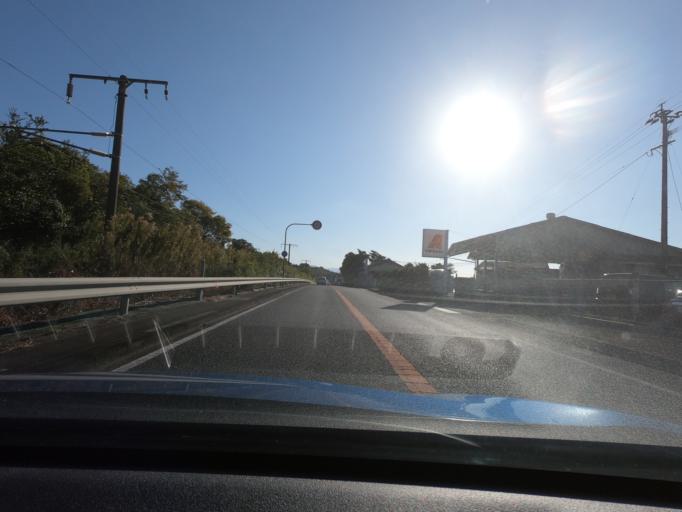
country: JP
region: Kagoshima
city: Izumi
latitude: 32.1416
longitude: 130.3551
